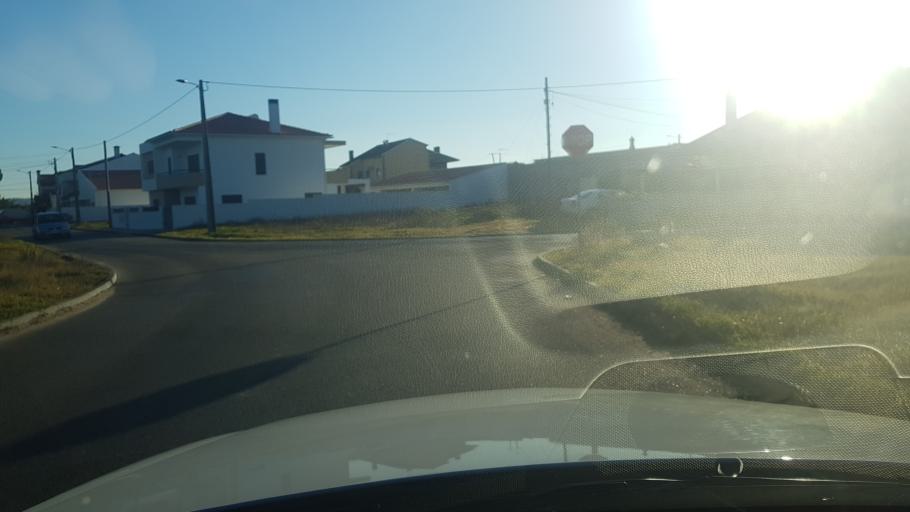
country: PT
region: Santarem
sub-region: Entroncamento
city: Entroncamento
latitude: 39.4769
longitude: -8.4828
